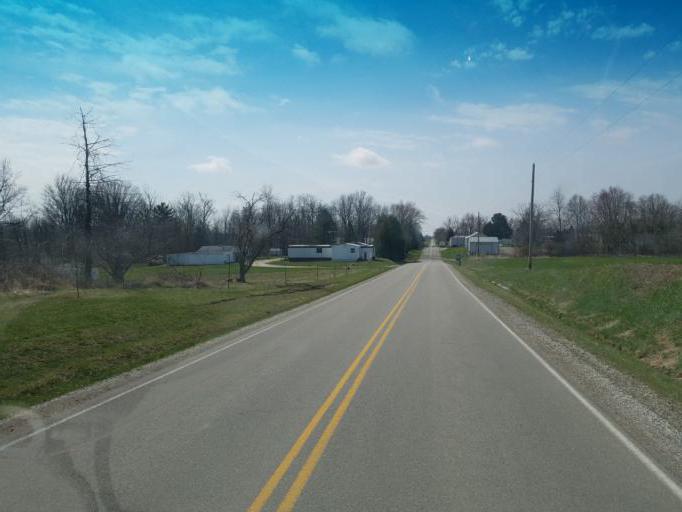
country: US
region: Ohio
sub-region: Crawford County
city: Bucyrus
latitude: 40.9299
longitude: -83.0933
